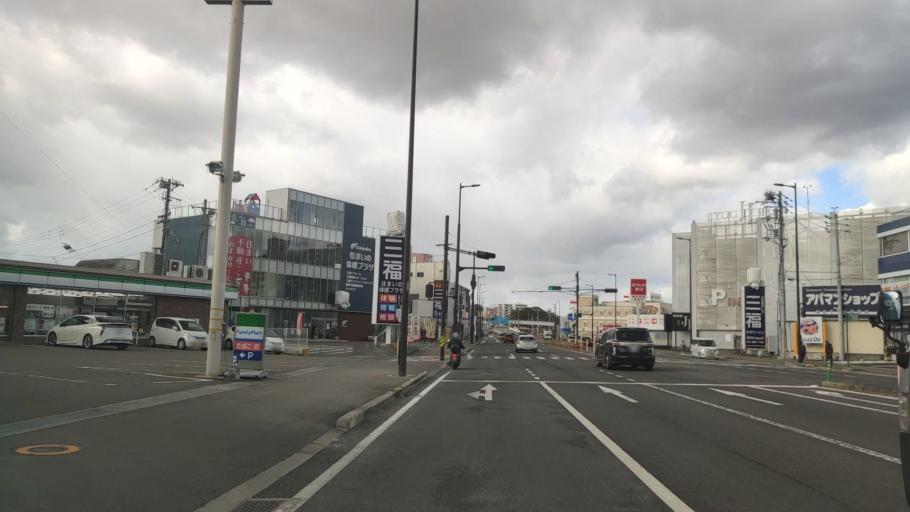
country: JP
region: Ehime
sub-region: Shikoku-chuo Shi
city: Matsuyama
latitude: 33.8315
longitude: 132.7794
